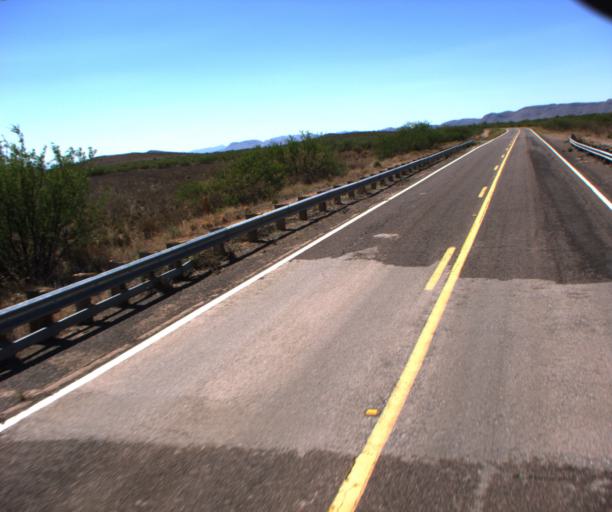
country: US
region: Arizona
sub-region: Cochise County
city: Douglas
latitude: 31.5176
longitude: -109.3069
